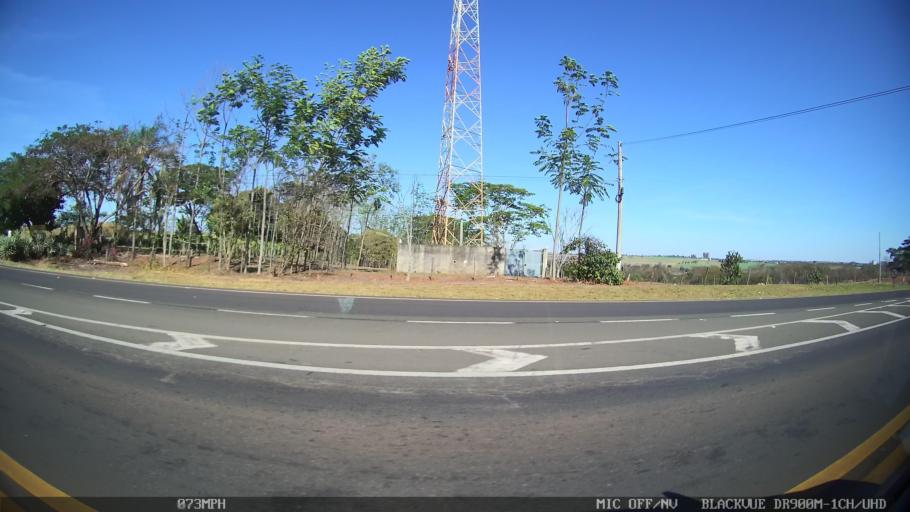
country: BR
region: Sao Paulo
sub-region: Olimpia
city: Olimpia
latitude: -20.6843
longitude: -48.9035
